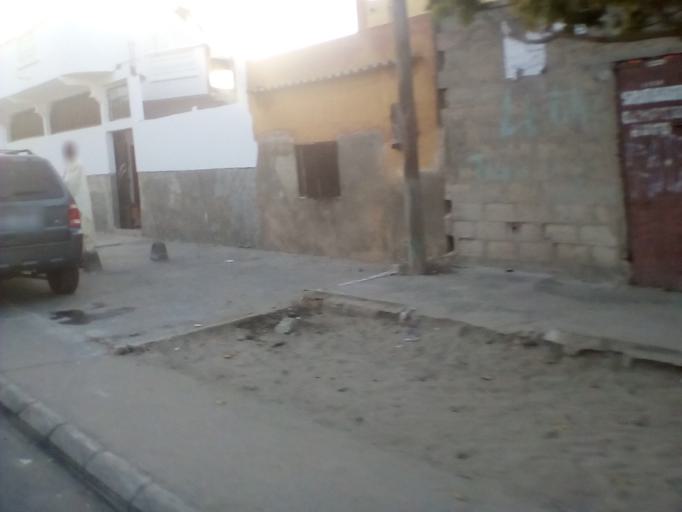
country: SN
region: Saint-Louis
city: Saint-Louis
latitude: 16.0128
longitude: -16.4946
